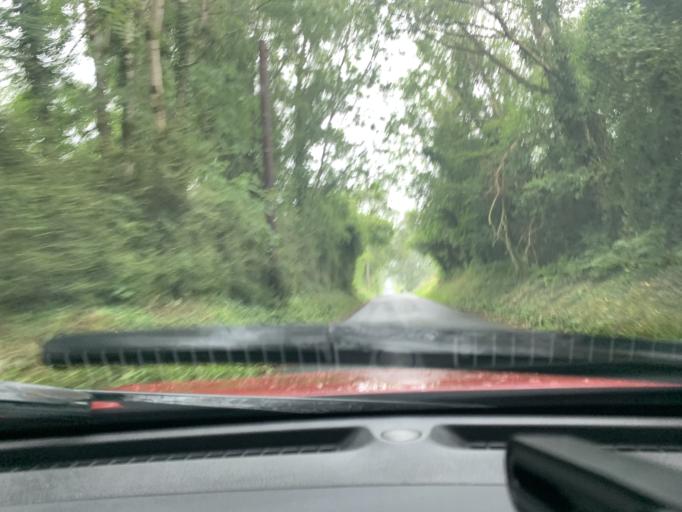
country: GB
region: Northern Ireland
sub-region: Fermanagh District
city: Enniskillen
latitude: 54.2892
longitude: -7.7102
